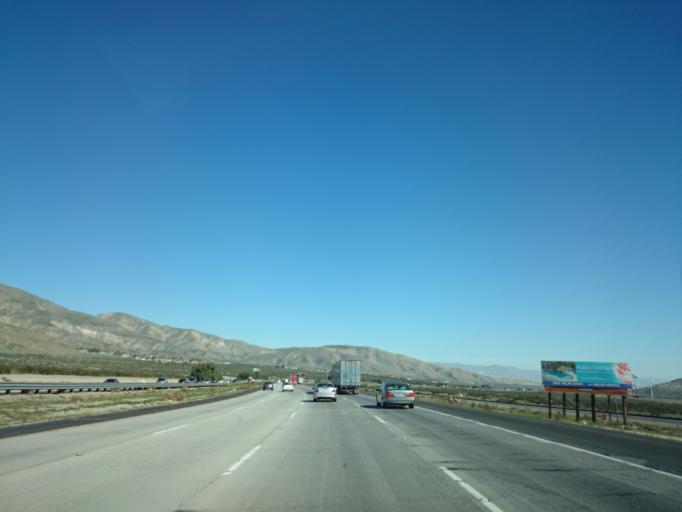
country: US
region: California
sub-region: Riverside County
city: Cabazon
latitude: 33.9216
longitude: -116.7461
